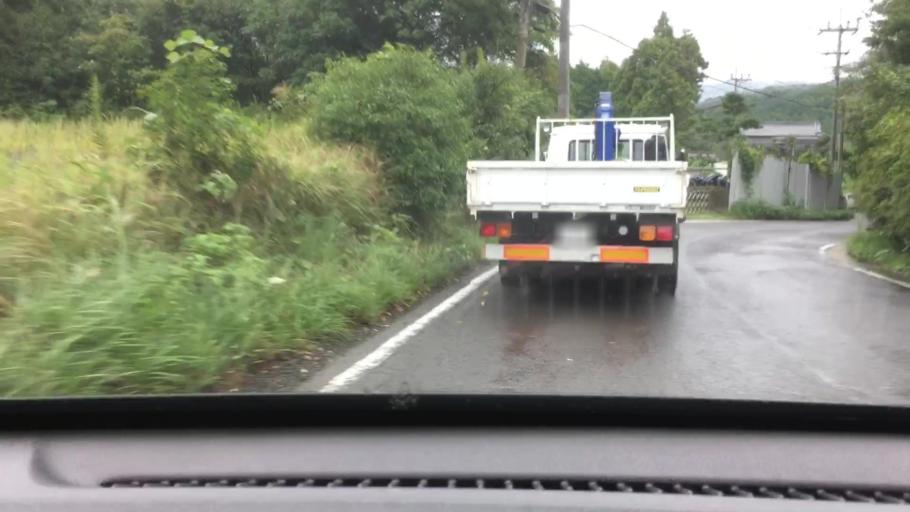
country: JP
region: Nagasaki
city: Togitsu
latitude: 32.8582
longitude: 129.7784
